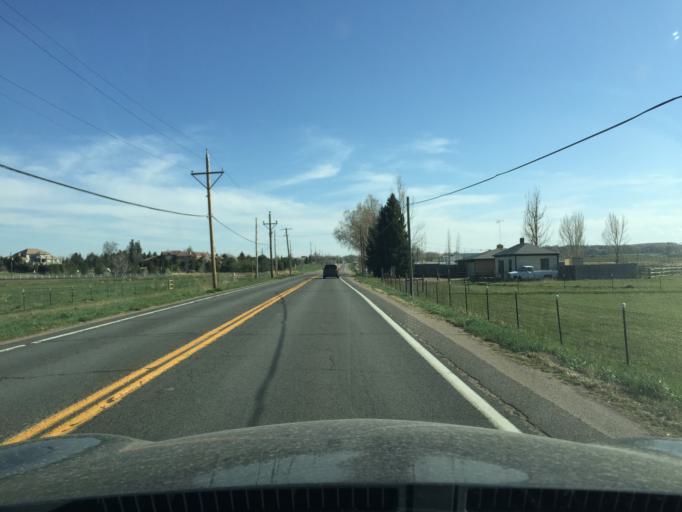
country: US
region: Colorado
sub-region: Boulder County
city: Niwot
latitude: 40.1183
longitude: -105.1311
